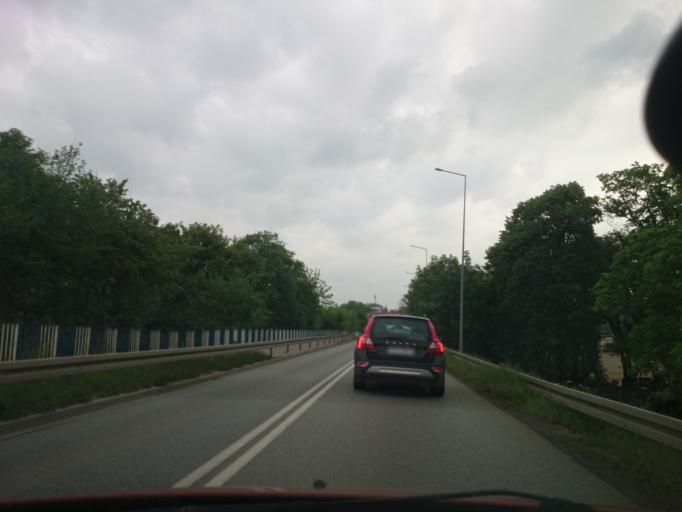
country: PL
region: Opole Voivodeship
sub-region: Powiat opolski
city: Czarnowasy
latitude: 50.7169
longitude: 17.9026
